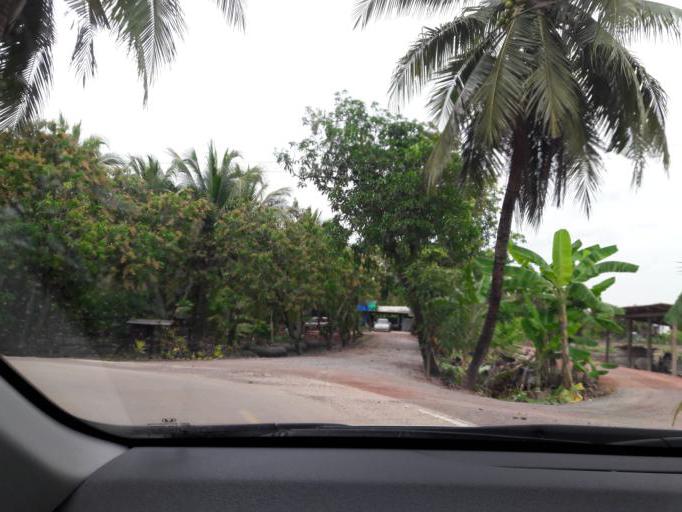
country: TH
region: Ratchaburi
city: Damnoen Saduak
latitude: 13.5502
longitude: 99.9897
